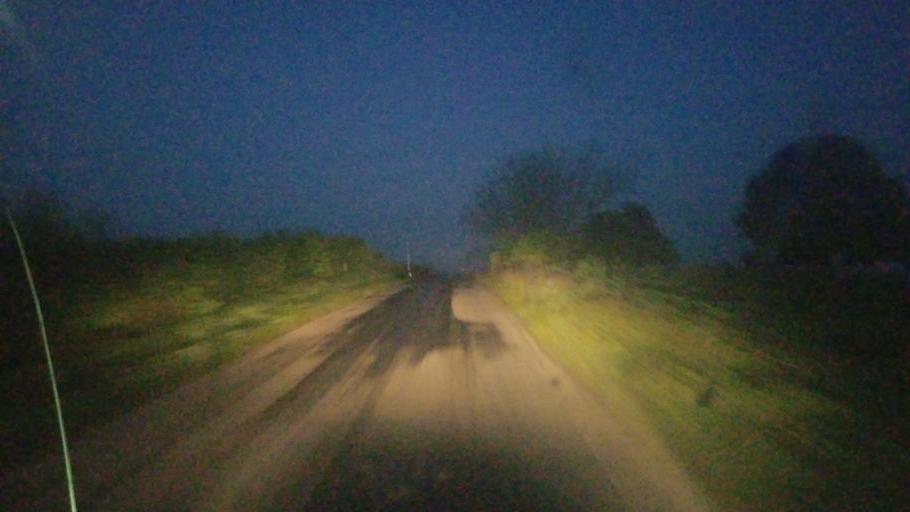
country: US
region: Ohio
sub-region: Perry County
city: Thornport
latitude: 39.9189
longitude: -82.3521
